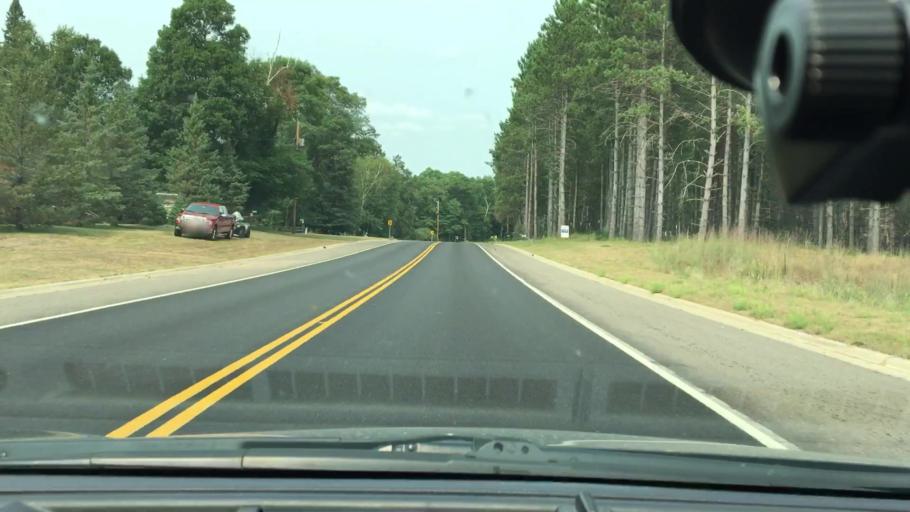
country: US
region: Minnesota
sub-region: Crow Wing County
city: Cross Lake
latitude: 46.7042
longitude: -94.0588
